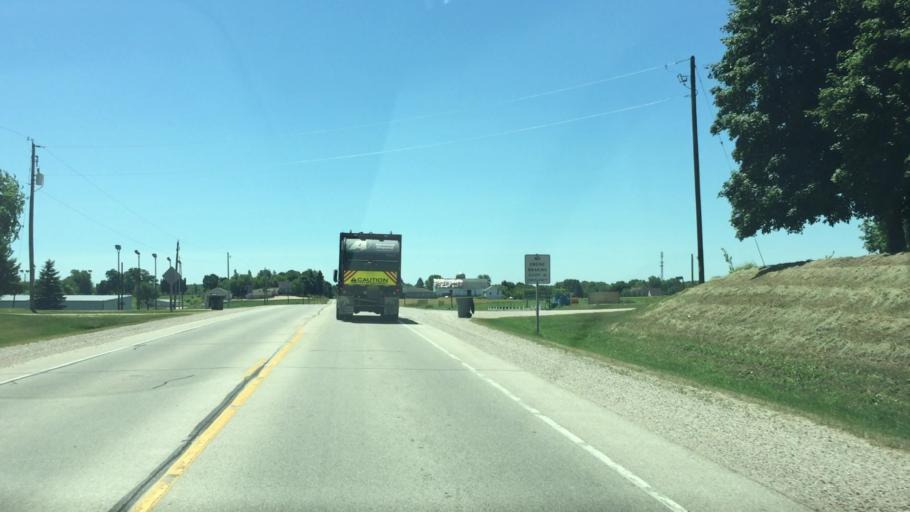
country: US
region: Wisconsin
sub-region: Calumet County
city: Chilton
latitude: 44.0470
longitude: -88.1630
